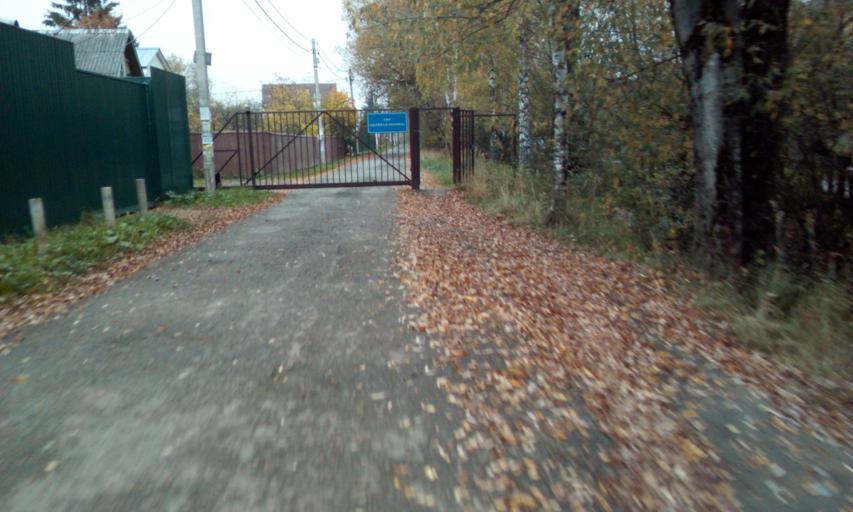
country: RU
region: Moskovskaya
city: Zhavoronki
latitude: 55.6497
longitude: 37.1084
